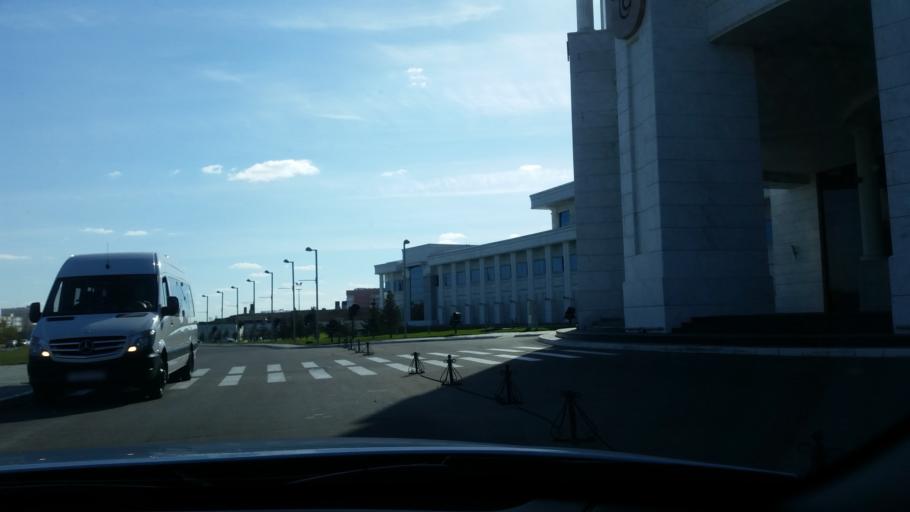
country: KZ
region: Astana Qalasy
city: Astana
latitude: 51.0902
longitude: 71.4012
